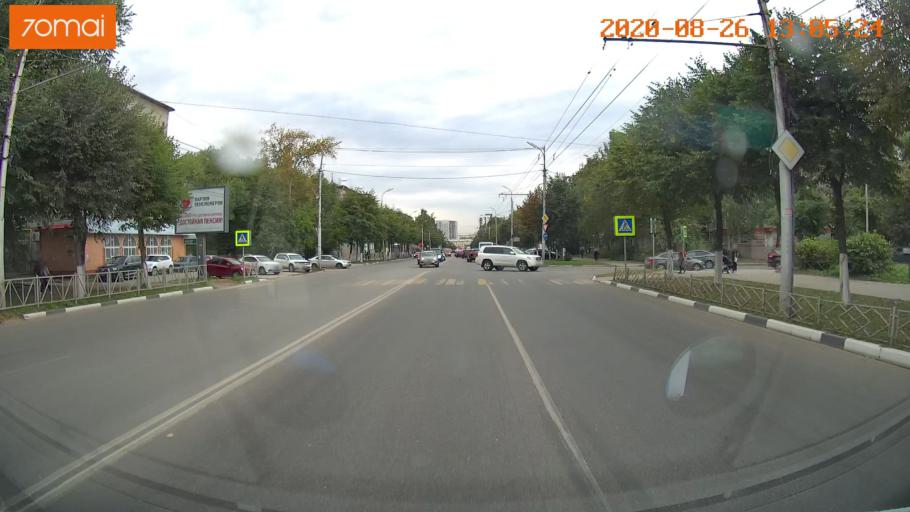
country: RU
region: Rjazan
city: Ryazan'
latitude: 54.6197
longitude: 39.7252
